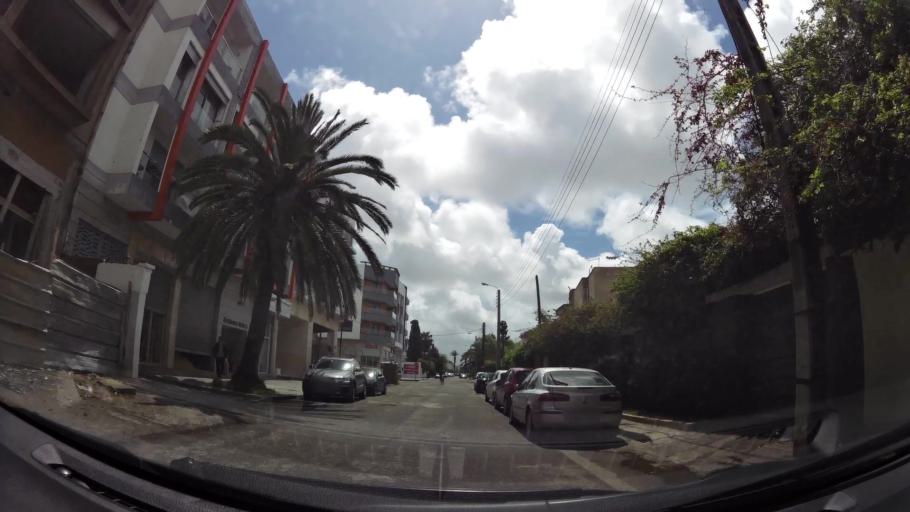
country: MA
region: Grand Casablanca
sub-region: Casablanca
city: Casablanca
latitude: 33.5676
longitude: -7.6380
